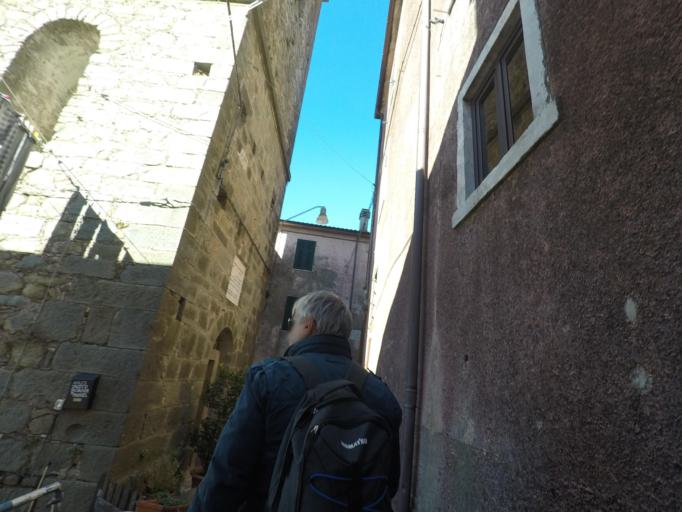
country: IT
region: Liguria
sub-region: Provincia di La Spezia
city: Casano-Dogana-Isola
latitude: 44.1108
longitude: 10.0757
